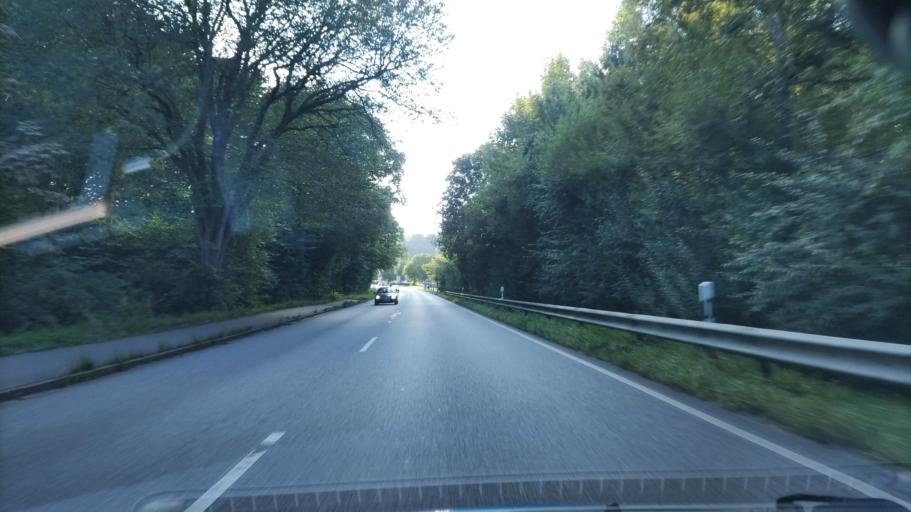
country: DE
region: Schleswig-Holstein
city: Bosdorf
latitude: 54.1456
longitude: 10.4614
